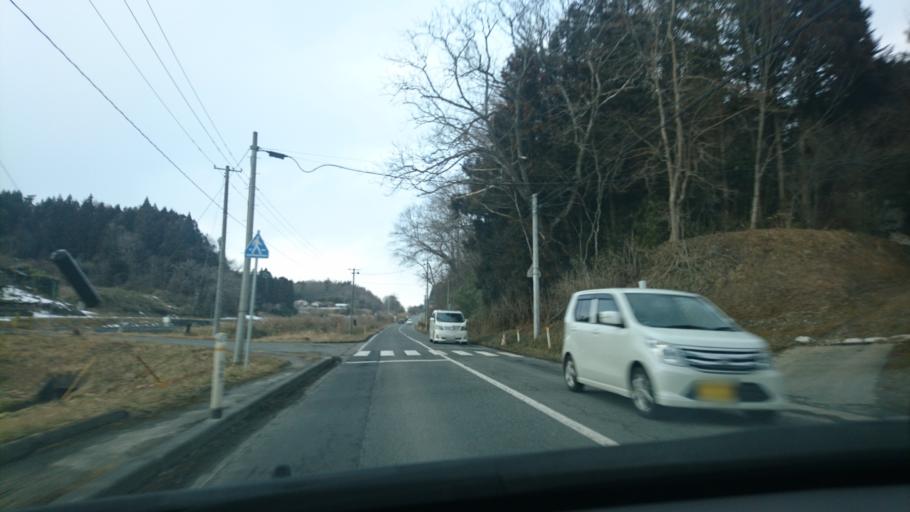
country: JP
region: Iwate
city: Ichinoseki
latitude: 38.9629
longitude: 141.3348
